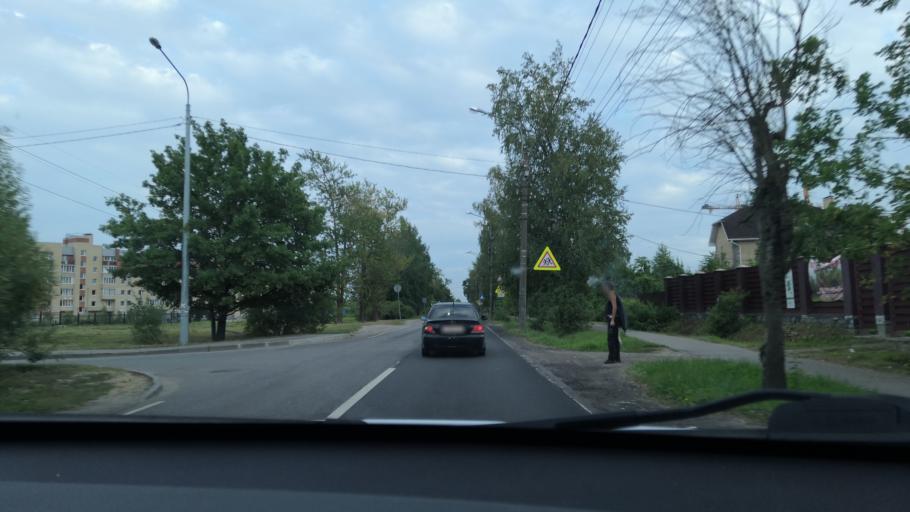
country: RU
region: St.-Petersburg
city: Pushkin
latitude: 59.6981
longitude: 30.4108
